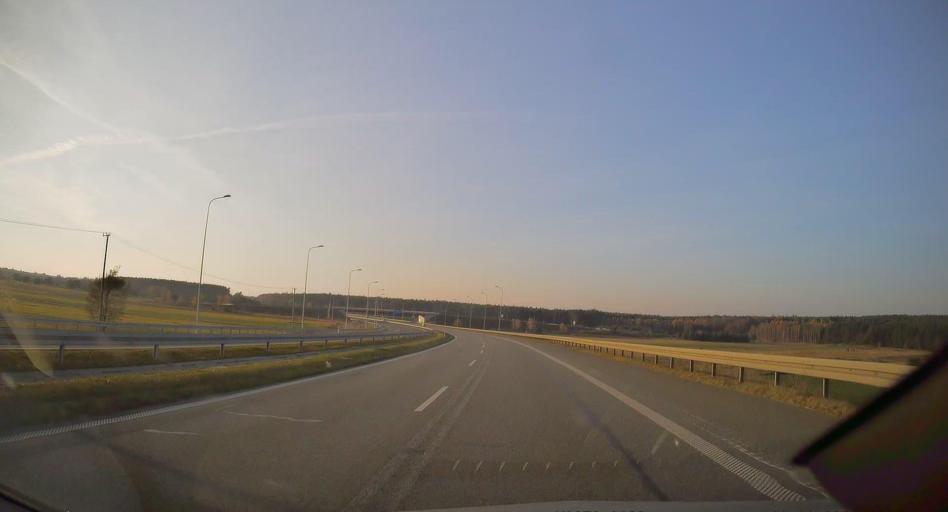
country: PL
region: Silesian Voivodeship
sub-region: Powiat bedzinski
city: Mierzecice
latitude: 50.4492
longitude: 19.1343
